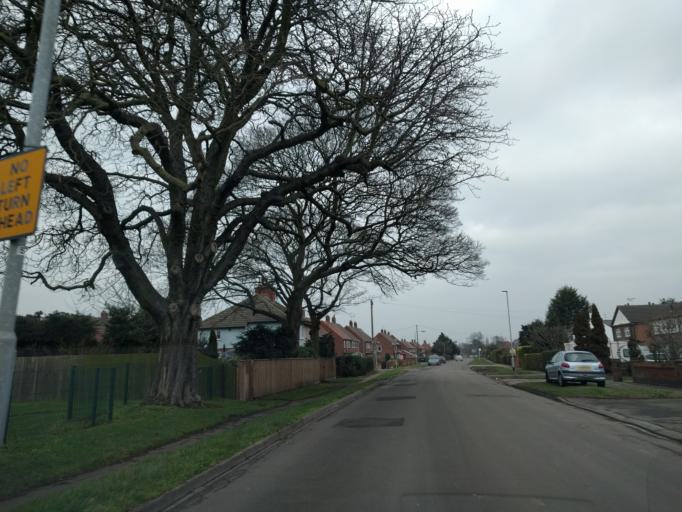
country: GB
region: England
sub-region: Nottinghamshire
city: Newark on Trent
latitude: 53.0873
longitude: -0.7994
